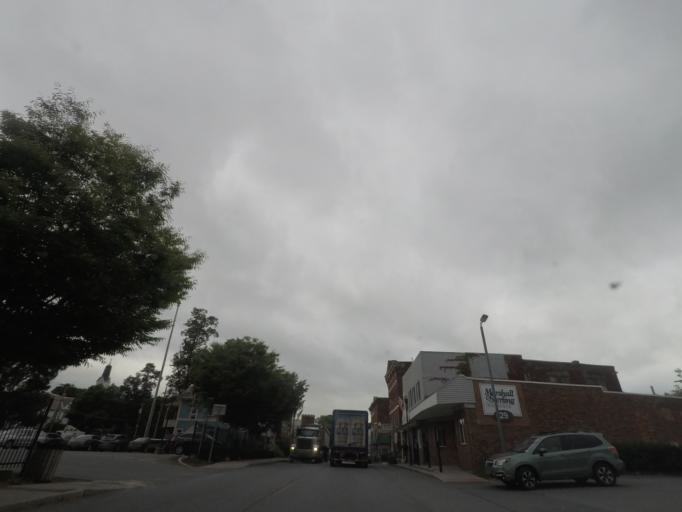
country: US
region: New York
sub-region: Rensselaer County
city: Hoosick Falls
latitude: 42.9010
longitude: -73.3518
